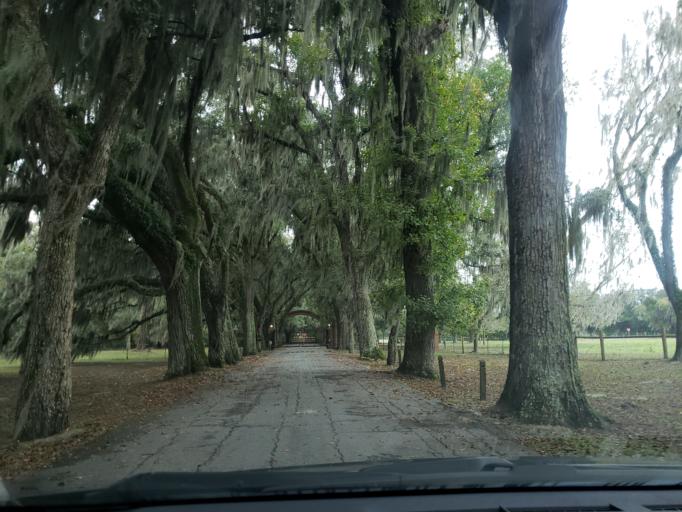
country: US
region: Georgia
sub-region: Chatham County
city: Montgomery
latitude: 31.9595
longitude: -81.0950
